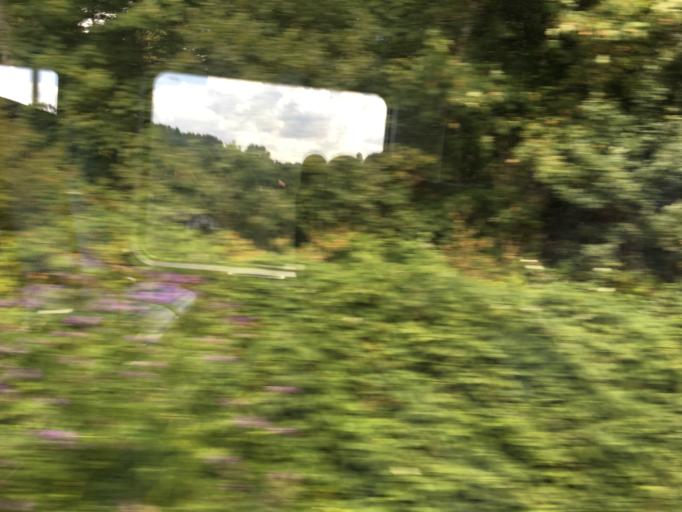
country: DE
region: North Rhine-Westphalia
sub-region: Regierungsbezirk Arnsberg
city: Bochum
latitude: 51.4847
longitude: 7.2585
